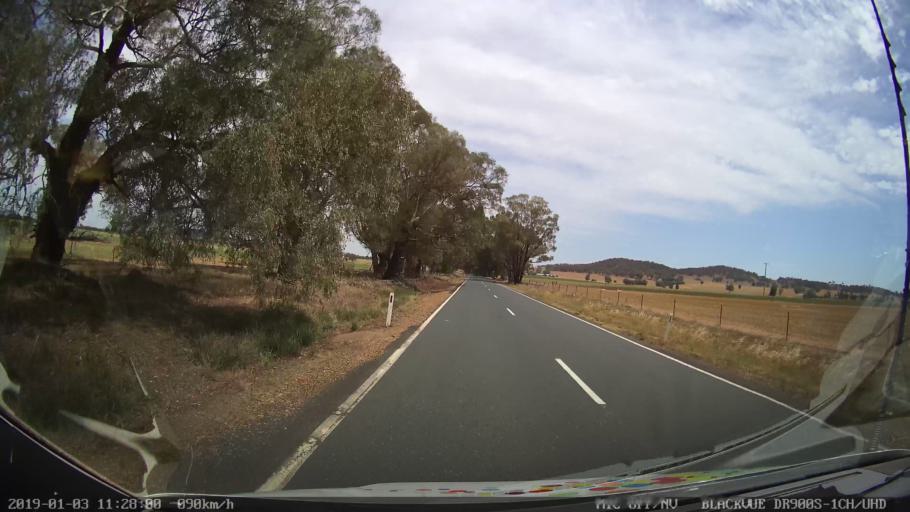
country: AU
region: New South Wales
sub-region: Weddin
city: Grenfell
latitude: -34.0064
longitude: 148.2140
